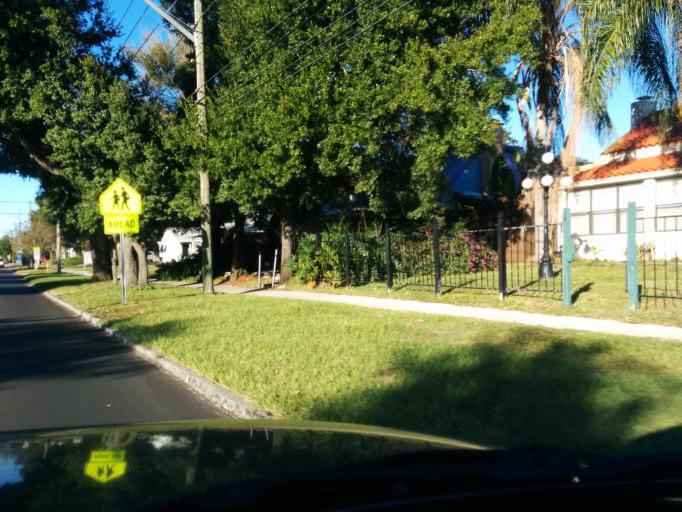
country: US
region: Florida
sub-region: Pinellas County
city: Saint Petersburg
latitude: 27.7905
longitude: -82.6549
